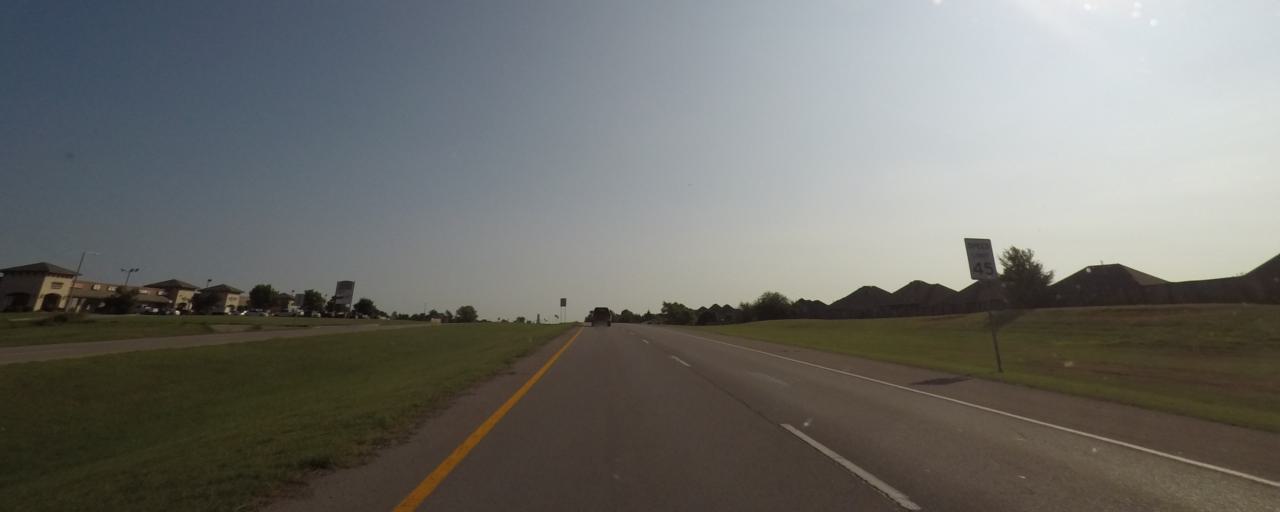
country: US
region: Oklahoma
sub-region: McClain County
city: Blanchard
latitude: 35.1408
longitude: -97.6496
